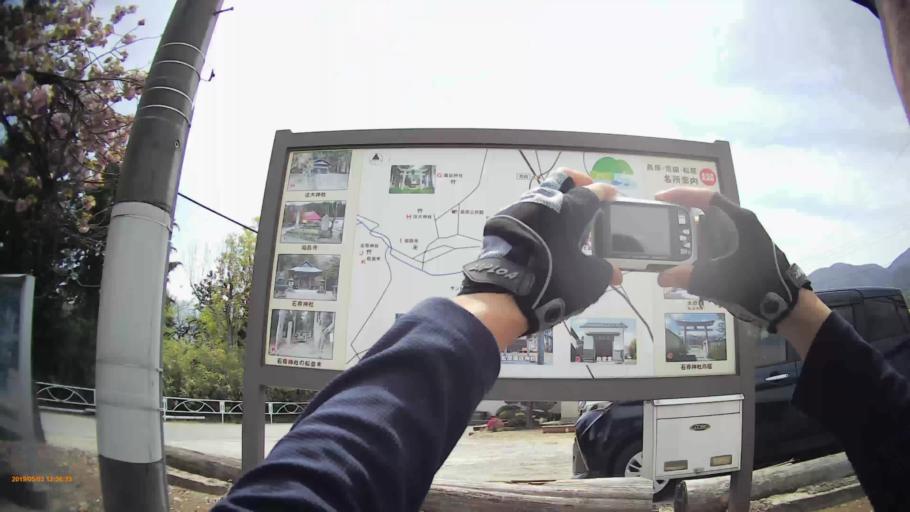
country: JP
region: Yamanashi
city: Nirasaki
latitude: 35.8443
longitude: 138.3006
